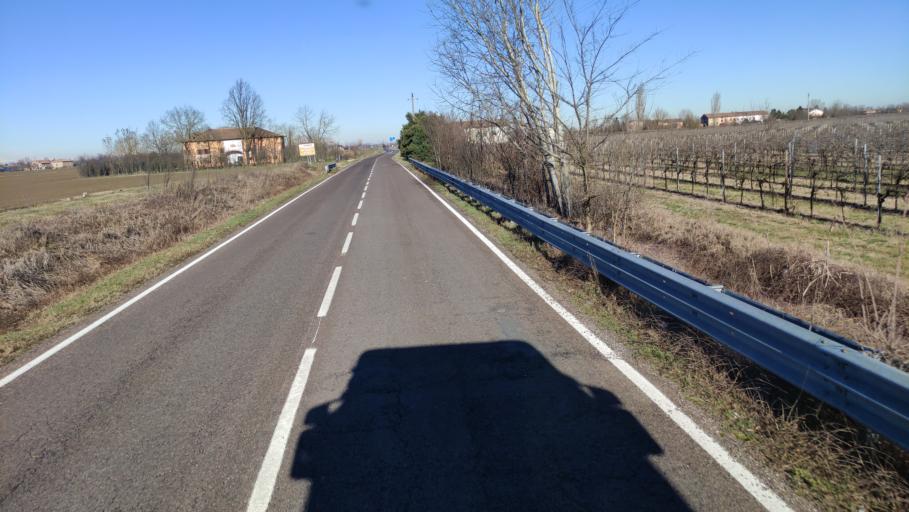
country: IT
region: Emilia-Romagna
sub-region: Provincia di Reggio Emilia
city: Rio Saliceto
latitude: 44.8137
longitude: 10.7857
